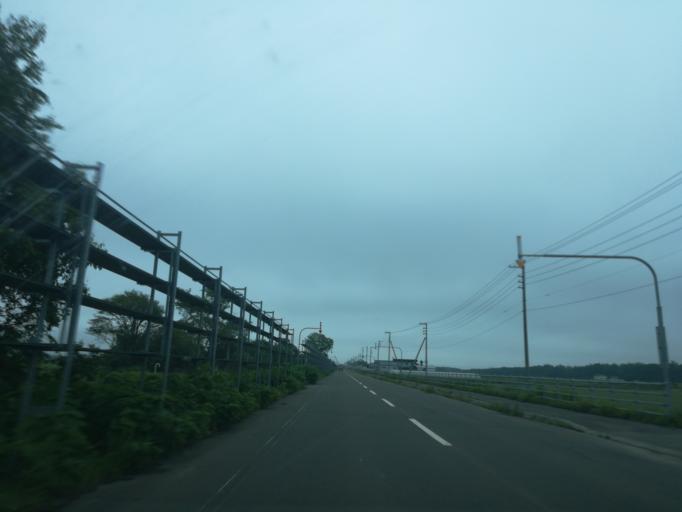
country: JP
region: Hokkaido
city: Ebetsu
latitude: 43.0510
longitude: 141.6052
